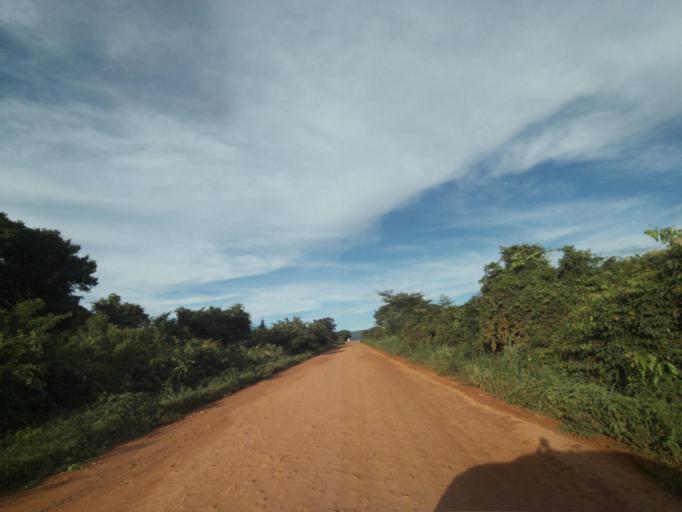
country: BR
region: Goias
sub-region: Jaragua
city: Jaragua
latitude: -15.8527
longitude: -49.3791
